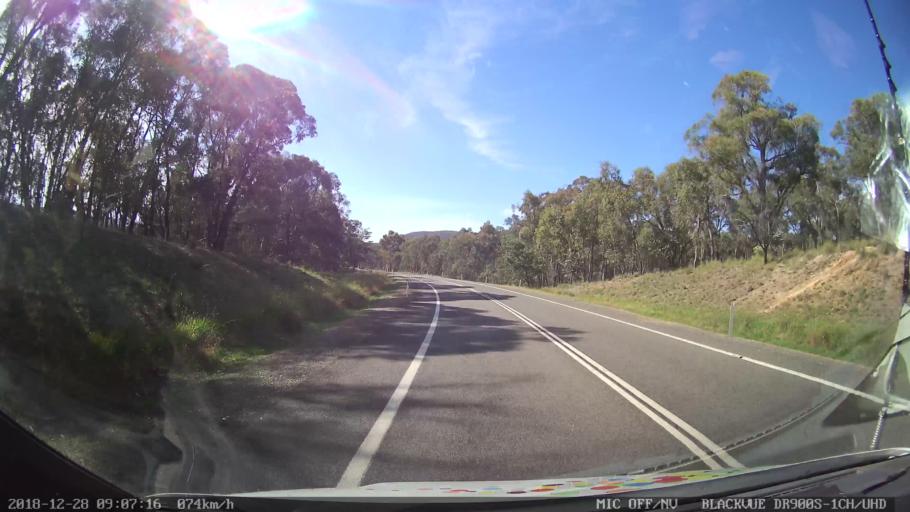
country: AU
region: New South Wales
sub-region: Upper Lachlan Shire
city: Crookwell
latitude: -34.2048
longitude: 149.3443
